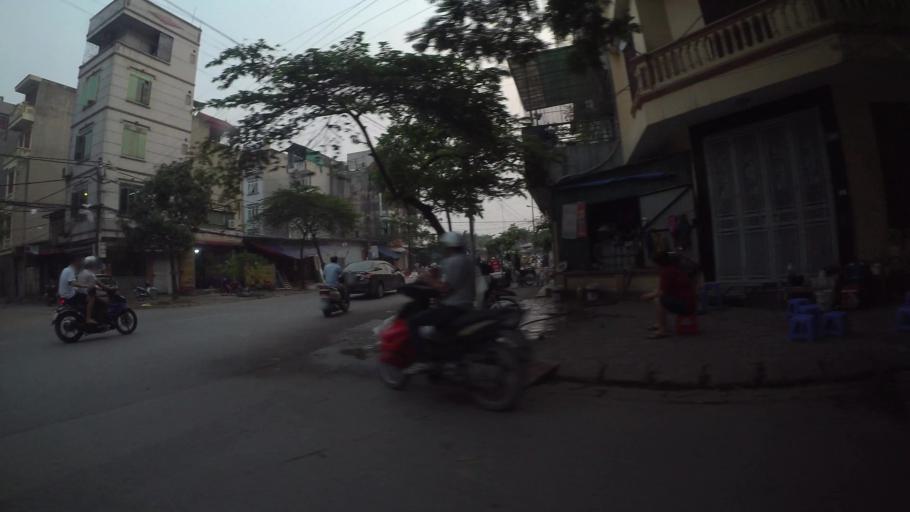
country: VN
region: Ha Noi
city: Thanh Xuan
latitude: 20.9771
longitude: 105.7967
